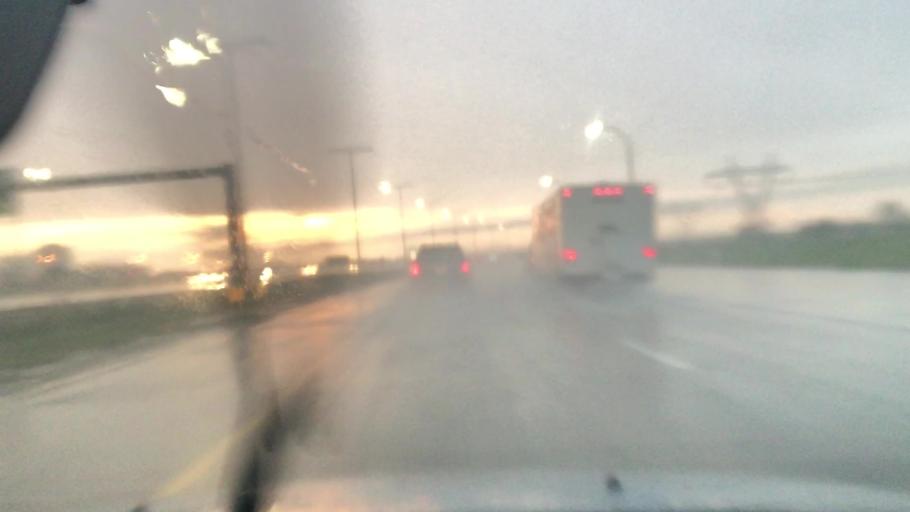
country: CA
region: Alberta
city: Devon
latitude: 53.4324
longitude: -113.5869
